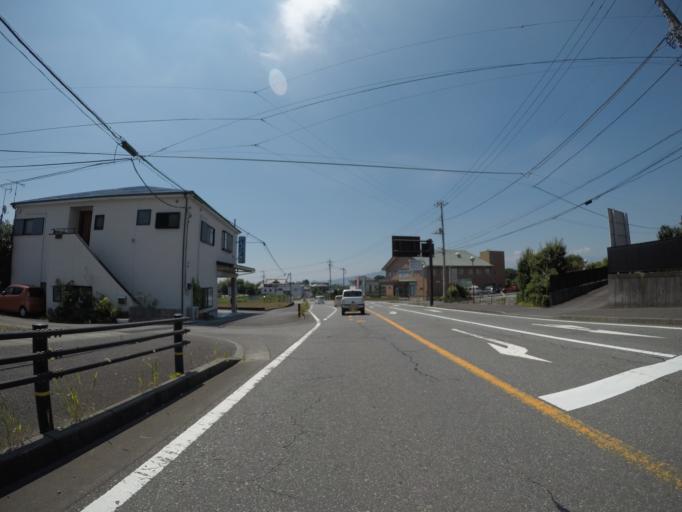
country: JP
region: Shizuoka
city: Fuji
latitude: 35.1975
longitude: 138.6815
